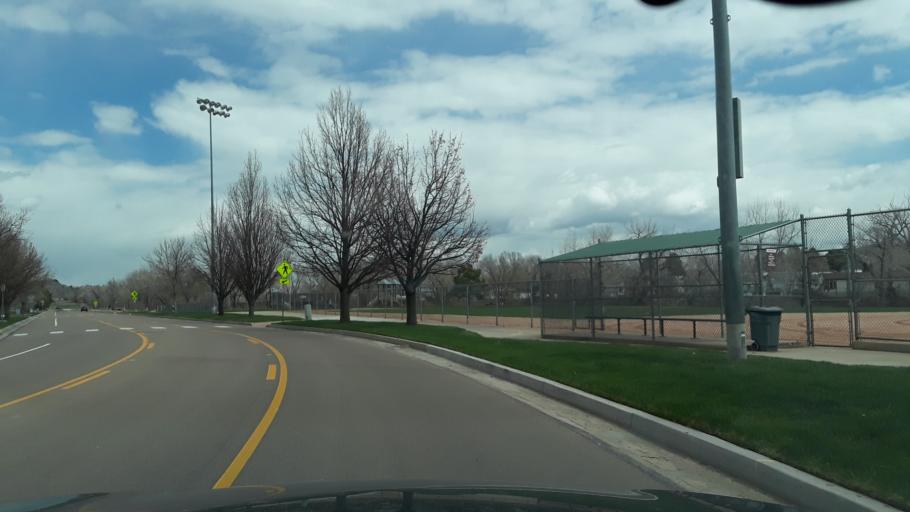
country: US
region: Colorado
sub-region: El Paso County
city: Colorado Springs
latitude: 38.8803
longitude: -104.8291
